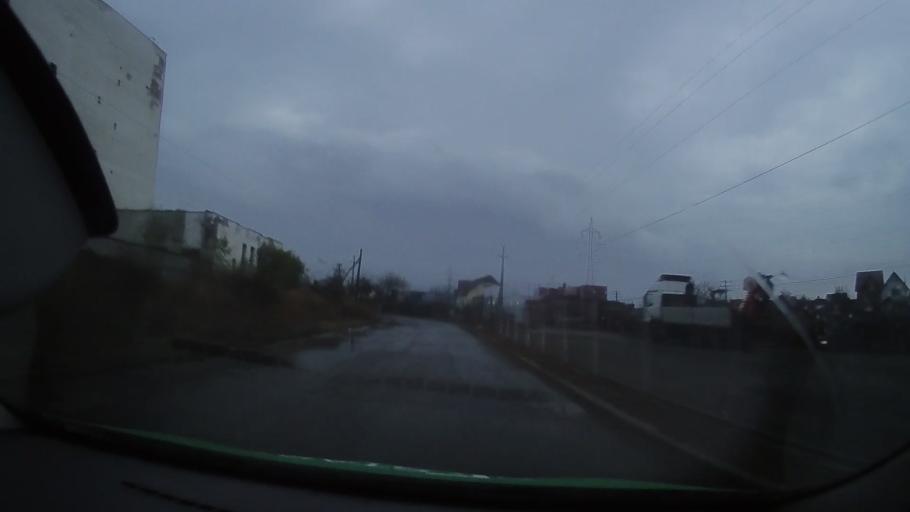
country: RO
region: Mures
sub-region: Municipiul Reghin
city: Iernuteni
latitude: 46.7672
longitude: 24.7223
